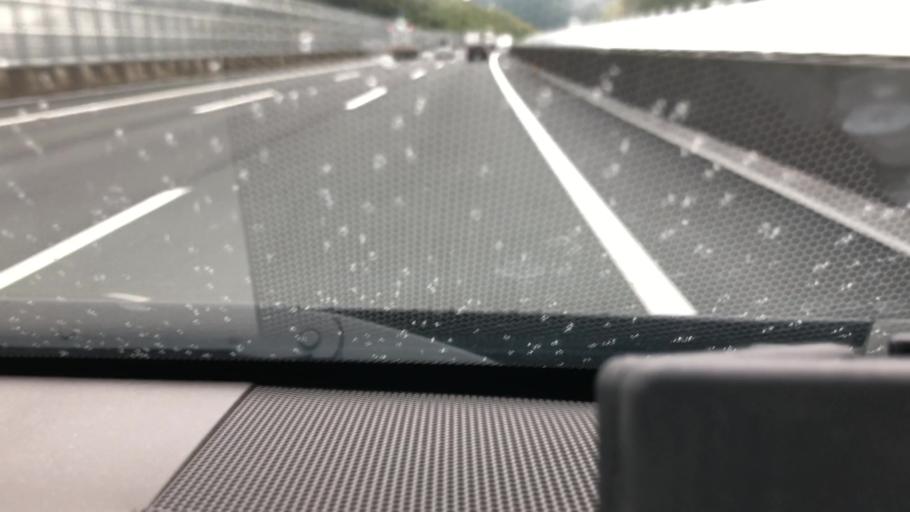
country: JP
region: Shizuoka
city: Shizuoka-shi
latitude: 35.0426
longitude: 138.3830
